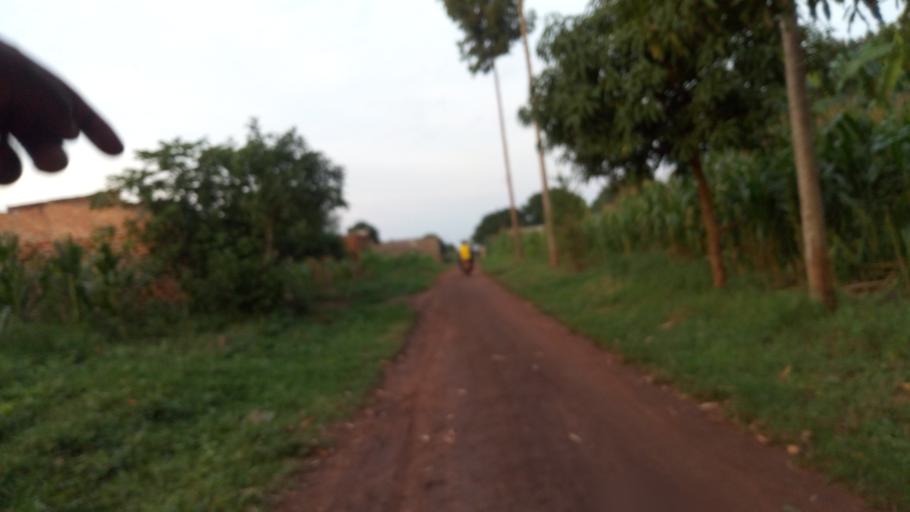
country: UG
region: Western Region
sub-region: Kiryandongo District
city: Kiryandongo
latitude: 1.8028
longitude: 32.0077
